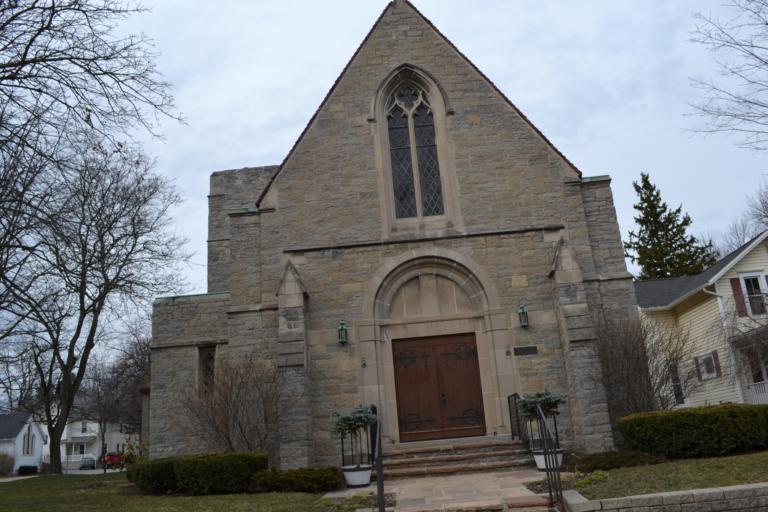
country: US
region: New York
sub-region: Erie County
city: East Aurora
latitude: 42.7679
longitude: -78.6139
